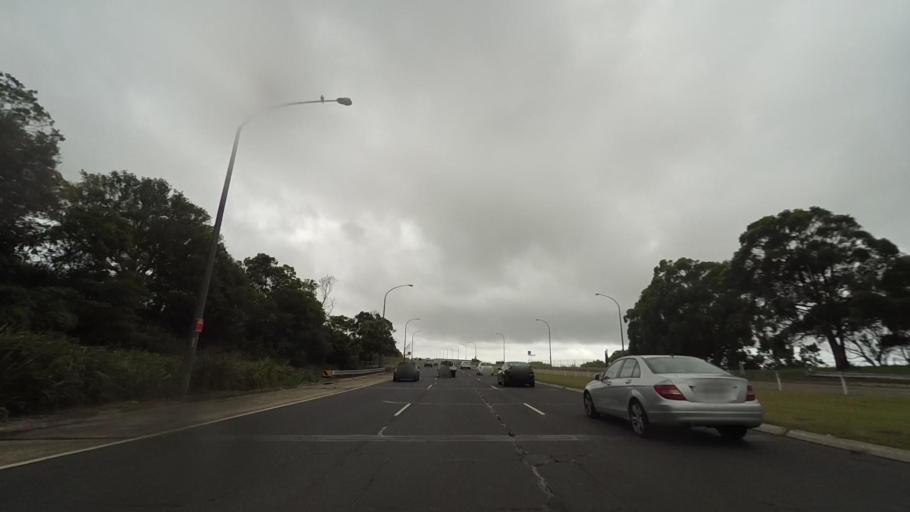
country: AU
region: New South Wales
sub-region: Rockdale
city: Dolls Point
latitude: -34.0117
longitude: 151.1259
